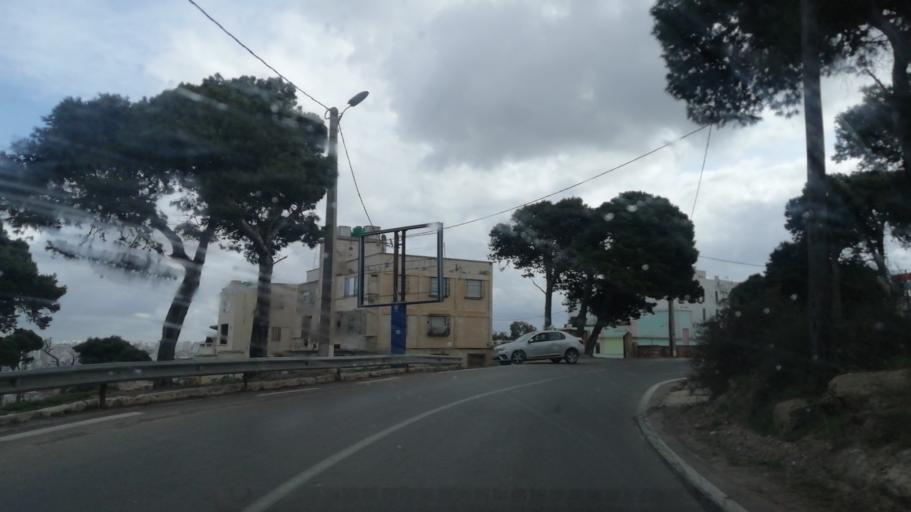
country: DZ
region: Oran
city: Oran
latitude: 35.7022
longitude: -0.6604
